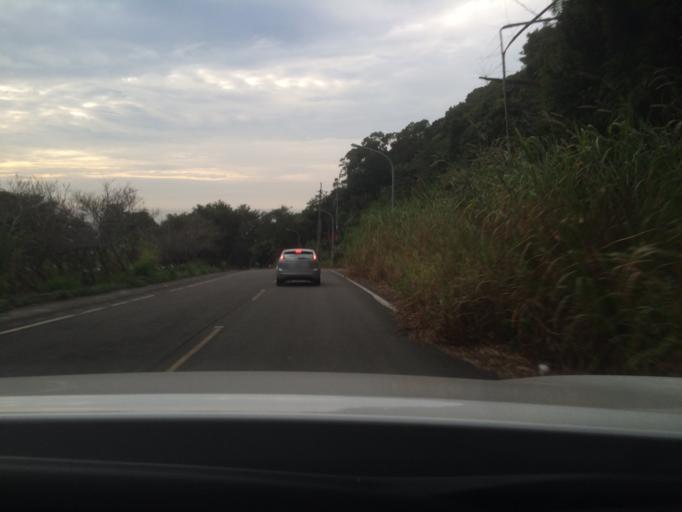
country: TW
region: Taiwan
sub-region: Nantou
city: Nantou
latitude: 23.9400
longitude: 120.6241
